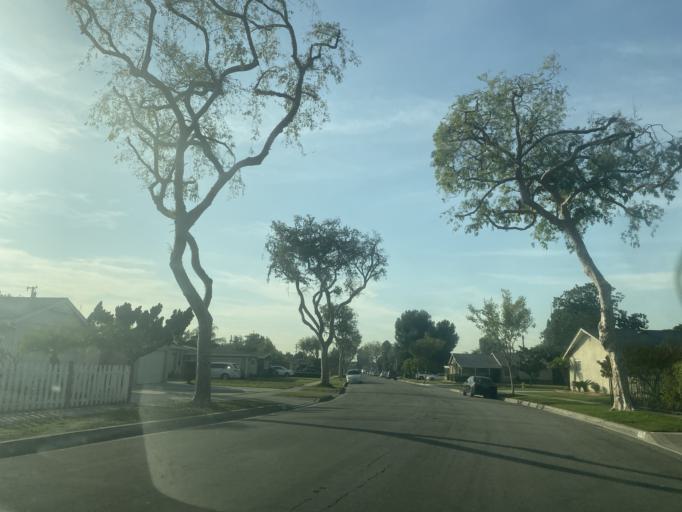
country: US
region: California
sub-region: Orange County
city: Buena Park
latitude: 33.8562
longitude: -117.9641
